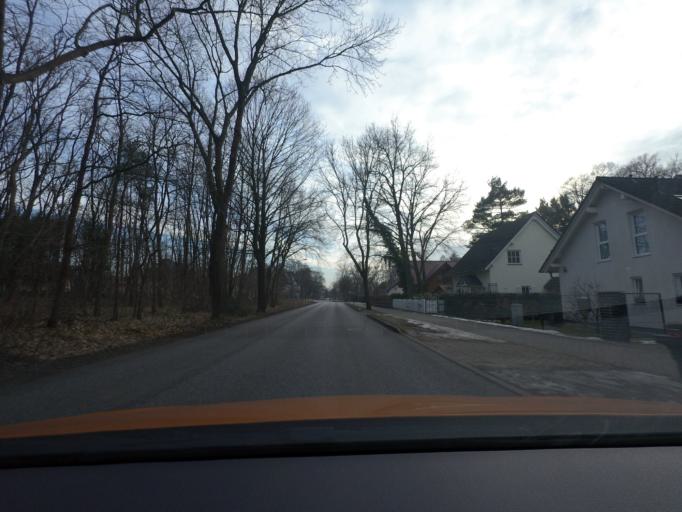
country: DE
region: Berlin
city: Blankenfelde
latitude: 52.6483
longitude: 13.3761
